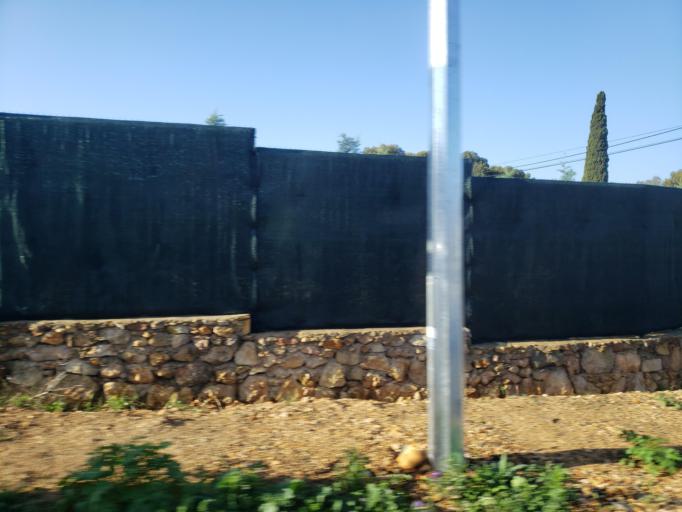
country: PT
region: Faro
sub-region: Portimao
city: Alvor
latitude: 37.1583
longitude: -8.5713
